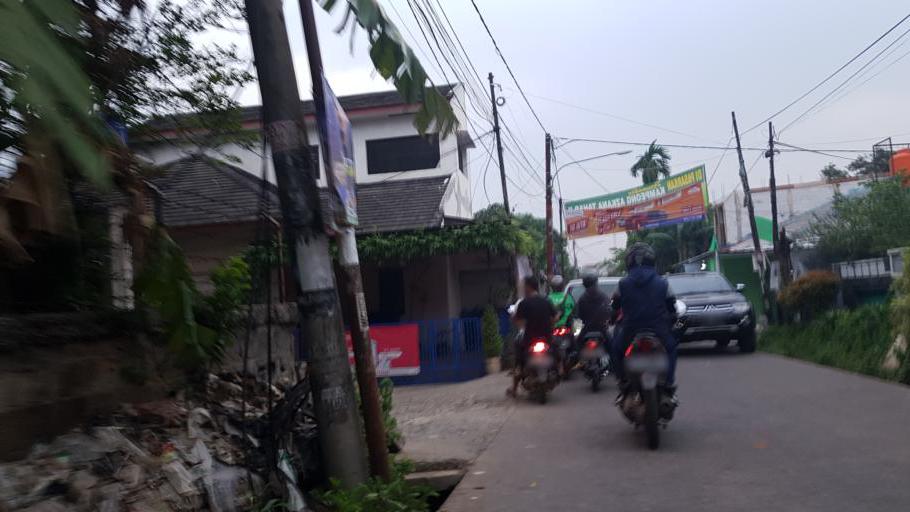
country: ID
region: West Java
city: Depok
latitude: -6.3670
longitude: 106.7960
